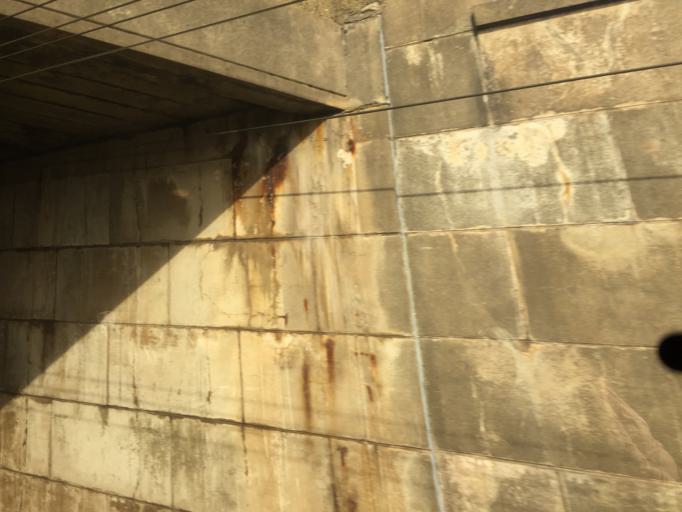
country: GB
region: Scotland
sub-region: South Lanarkshire
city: Carnwath
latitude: 55.6870
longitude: -3.6599
